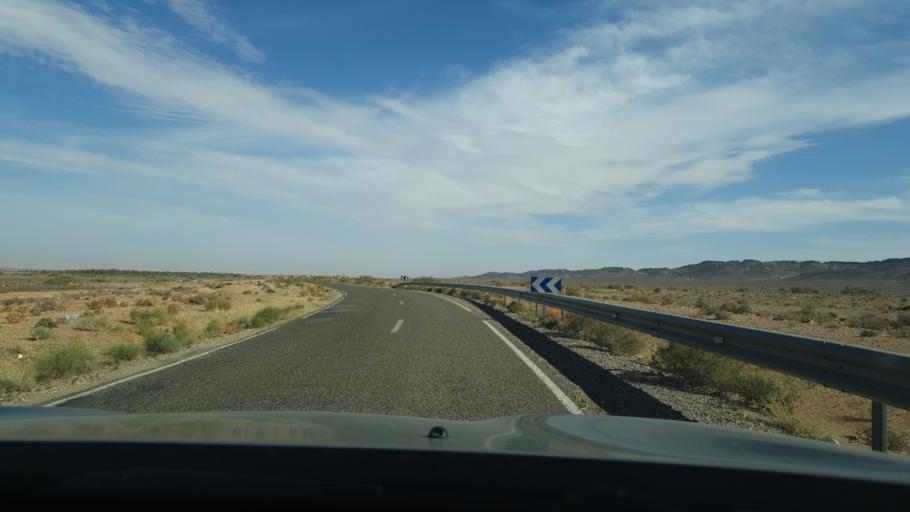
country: MA
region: Meknes-Tafilalet
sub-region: Errachidia
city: Goulmima
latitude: 31.5110
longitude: -4.9886
